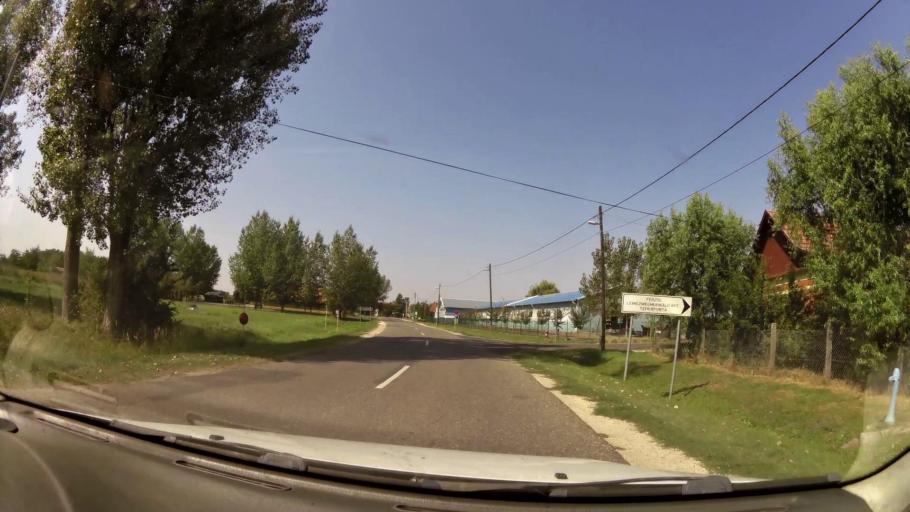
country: HU
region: Pest
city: Tapioszolos
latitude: 47.2833
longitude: 19.8687
